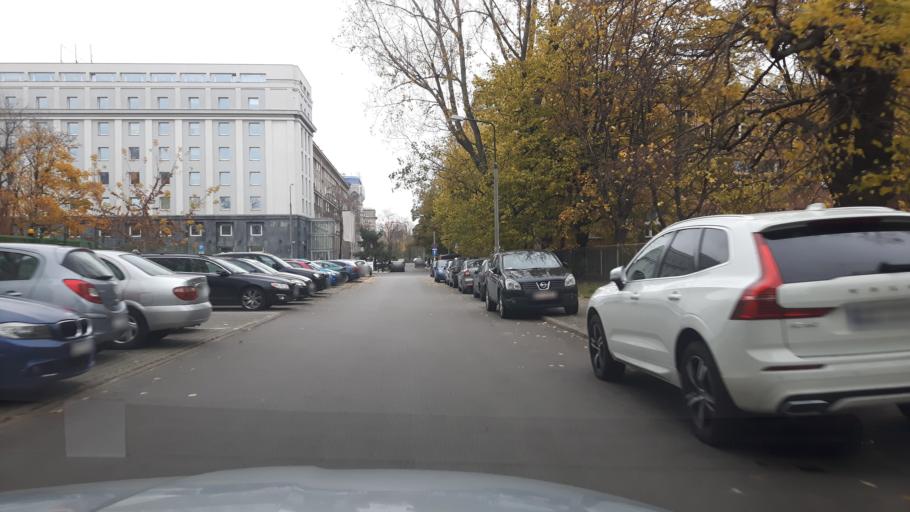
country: PL
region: Masovian Voivodeship
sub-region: Warszawa
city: Praga Polnoc
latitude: 52.2591
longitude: 21.0320
